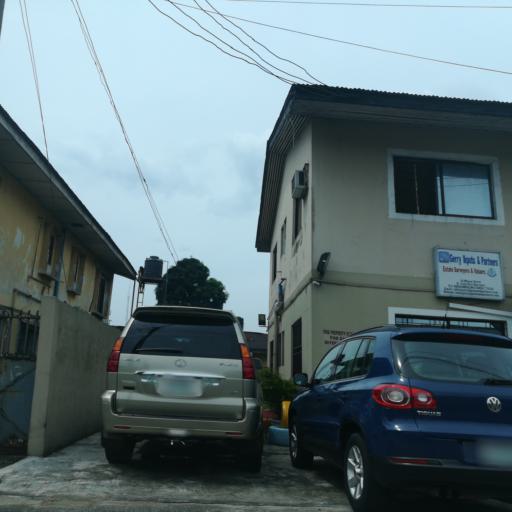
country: NG
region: Rivers
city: Port Harcourt
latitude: 4.8024
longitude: 7.0061
